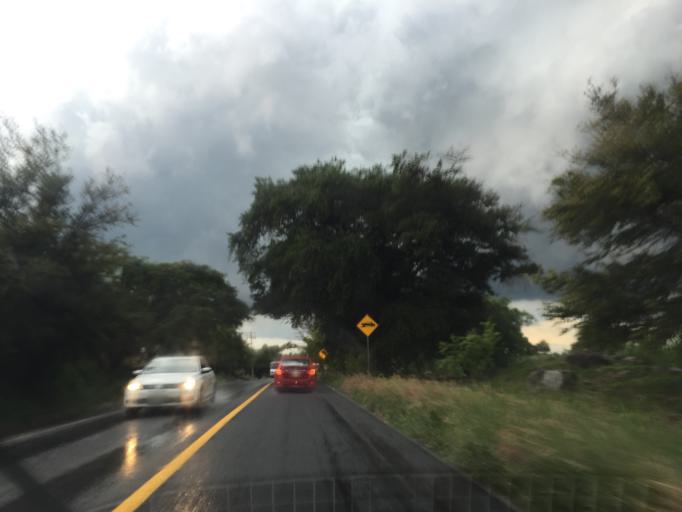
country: MX
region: Colima
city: Queseria
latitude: 19.3690
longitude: -103.5797
